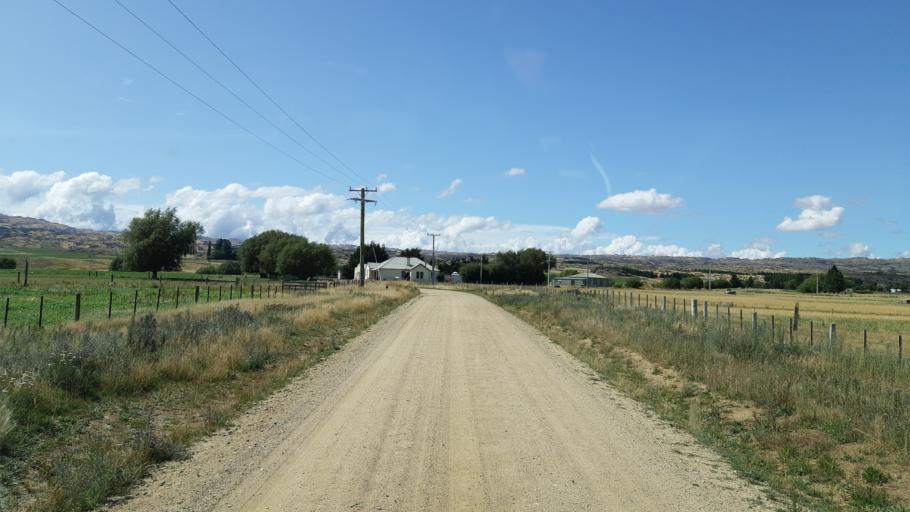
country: NZ
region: Otago
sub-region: Queenstown-Lakes District
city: Wanaka
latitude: -45.2131
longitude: 169.6829
